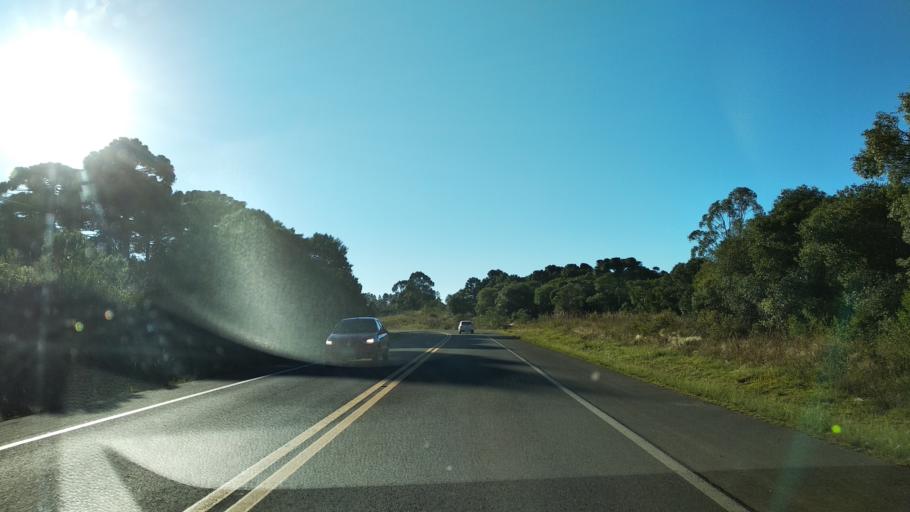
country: BR
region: Santa Catarina
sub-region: Lages
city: Lages
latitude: -27.7911
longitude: -50.4168
